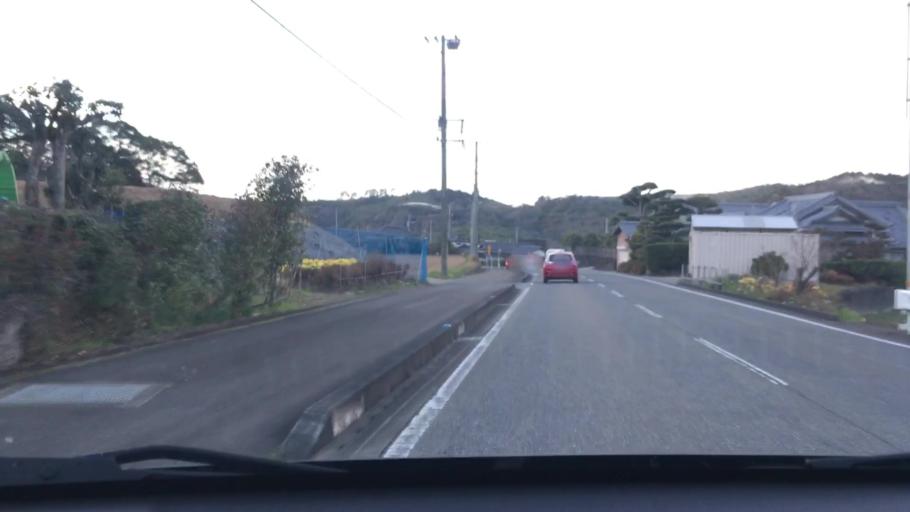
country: JP
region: Oita
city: Bungo-Takada-shi
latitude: 33.4993
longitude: 131.3757
